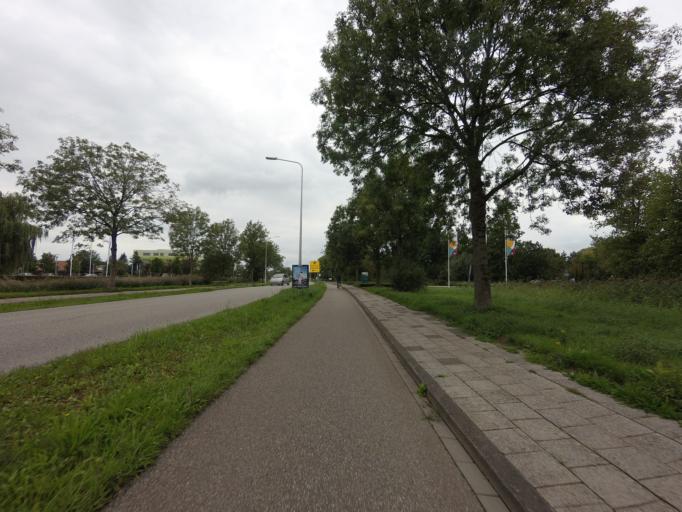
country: NL
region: Friesland
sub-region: Sudwest Fryslan
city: Sneek
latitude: 53.0378
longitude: 5.6457
